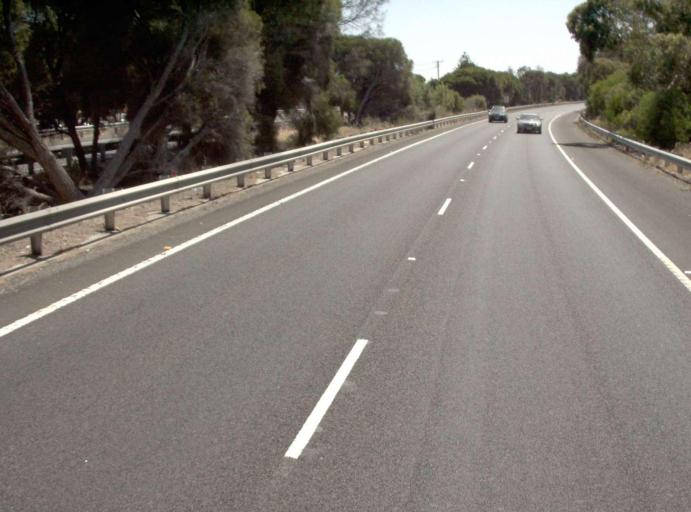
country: AU
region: Victoria
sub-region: Frankston
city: Frankston North
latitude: -38.1146
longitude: 145.1377
